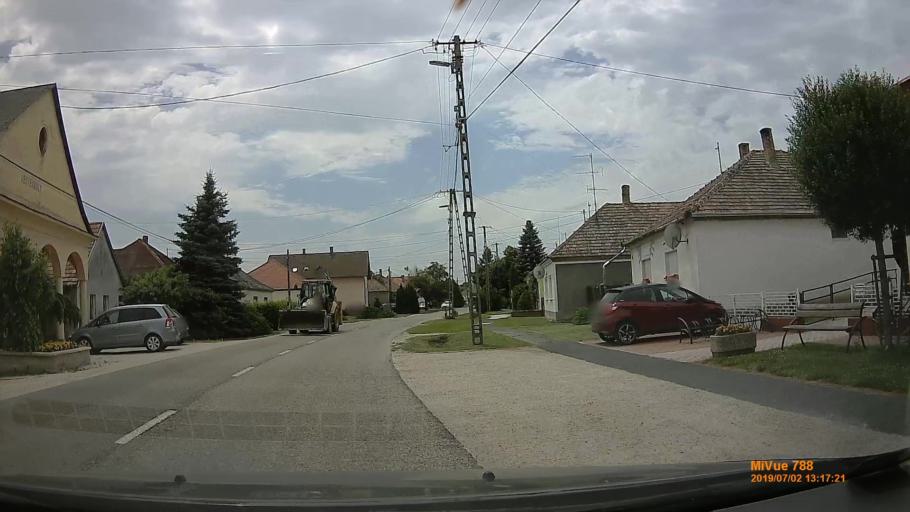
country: HU
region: Gyor-Moson-Sopron
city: Halaszi
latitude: 47.8615
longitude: 17.3240
